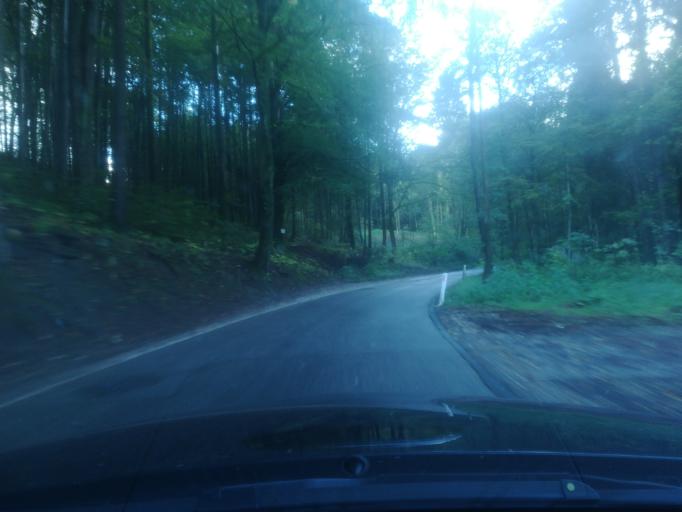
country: AT
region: Upper Austria
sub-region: Linz Stadt
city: Linz
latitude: 48.3431
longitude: 14.2680
